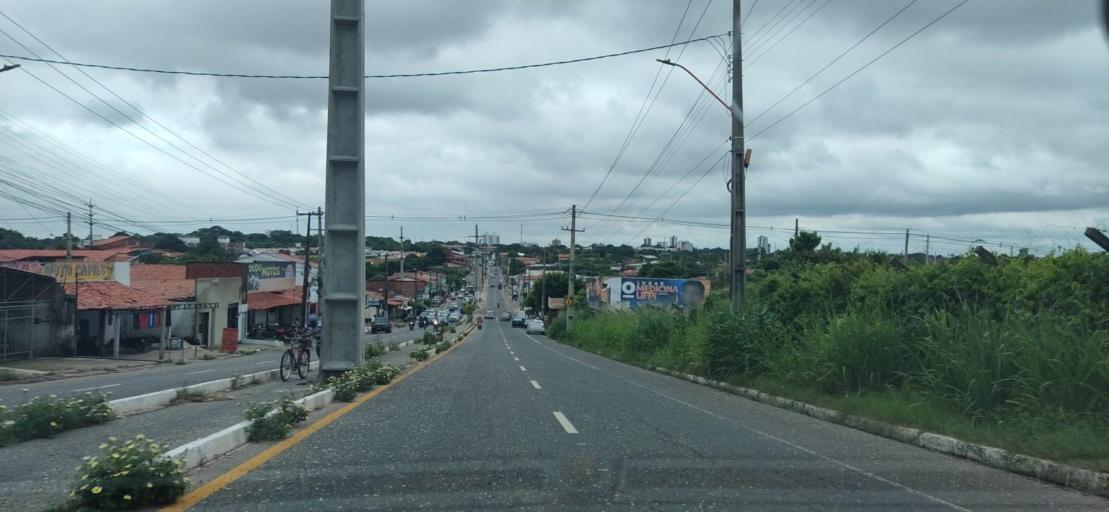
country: BR
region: Piaui
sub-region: Teresina
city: Teresina
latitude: -5.0577
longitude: -42.7499
